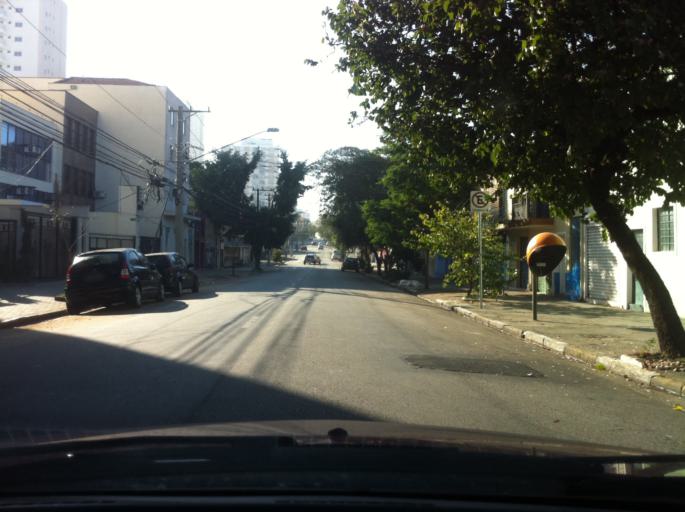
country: BR
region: Sao Paulo
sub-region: Sao Paulo
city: Sao Paulo
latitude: -23.6041
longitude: -46.6437
